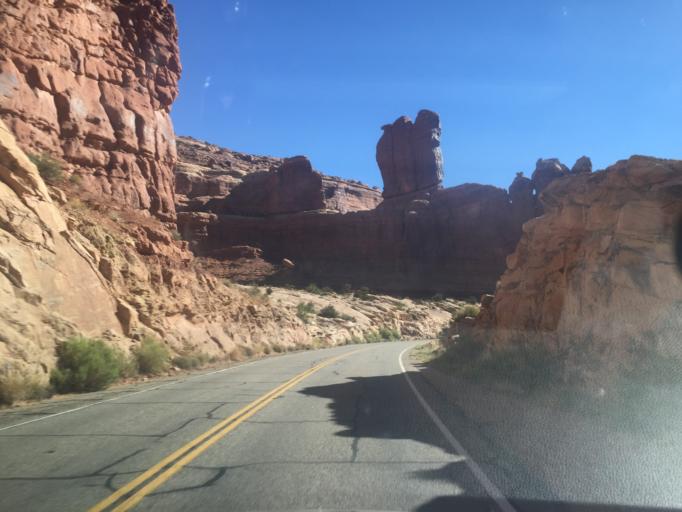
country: US
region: Utah
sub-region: Grand County
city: Moab
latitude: 38.6185
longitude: -109.6205
